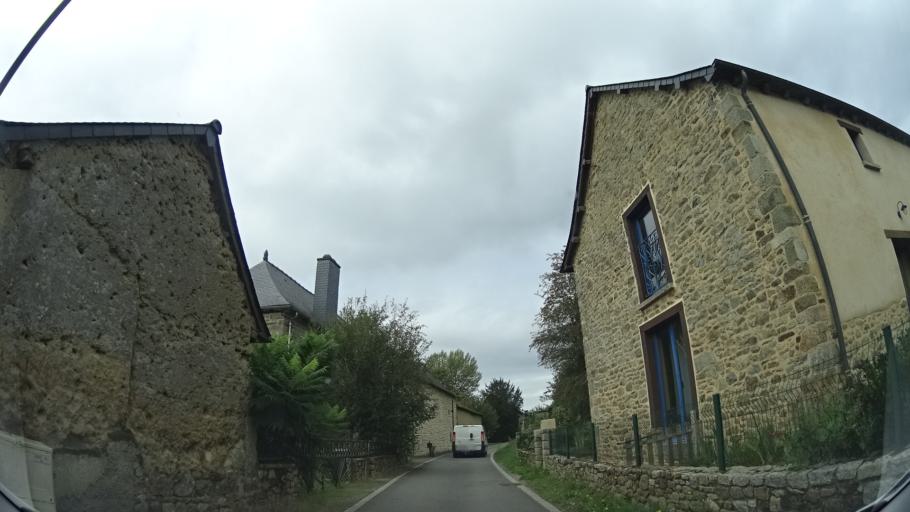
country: FR
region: Brittany
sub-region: Departement d'Ille-et-Vilaine
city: Romille
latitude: 48.2838
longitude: -1.8892
